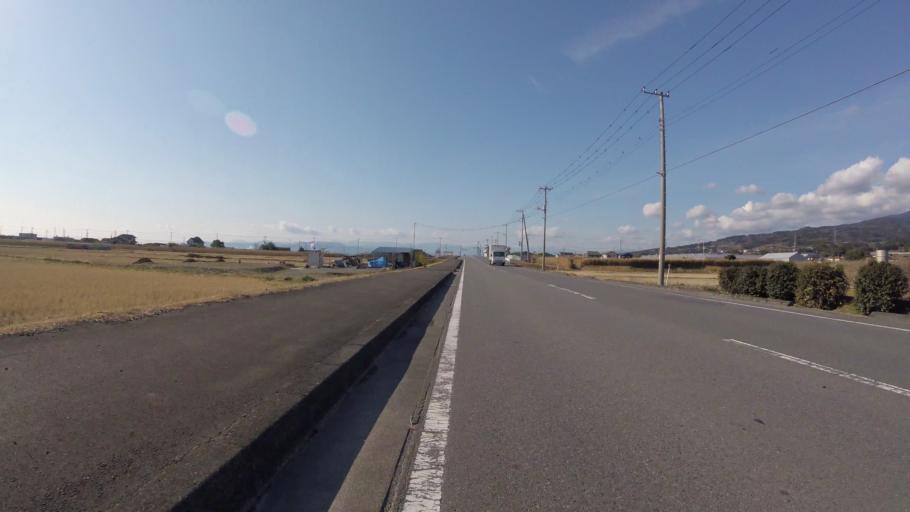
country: JP
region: Shizuoka
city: Numazu
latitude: 35.1443
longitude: 138.7801
